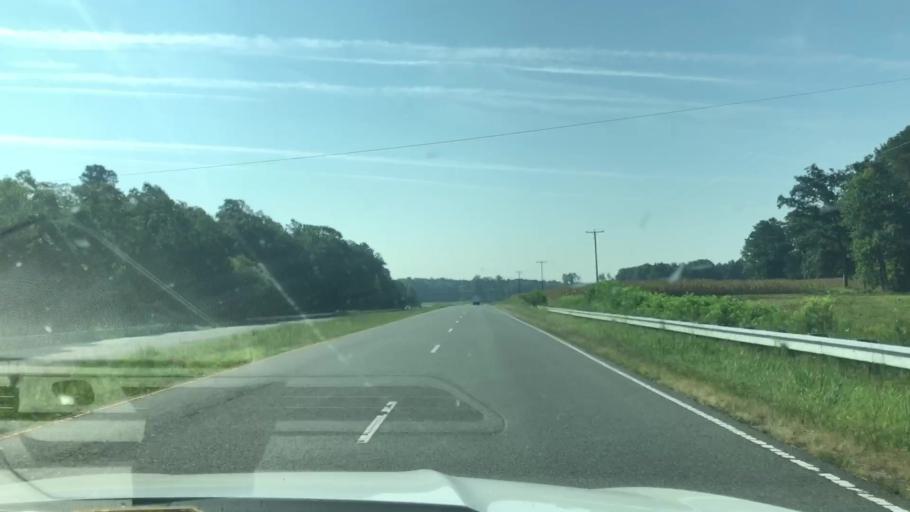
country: US
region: Virginia
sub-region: Richmond County
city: Warsaw
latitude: 37.9126
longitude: -76.6964
